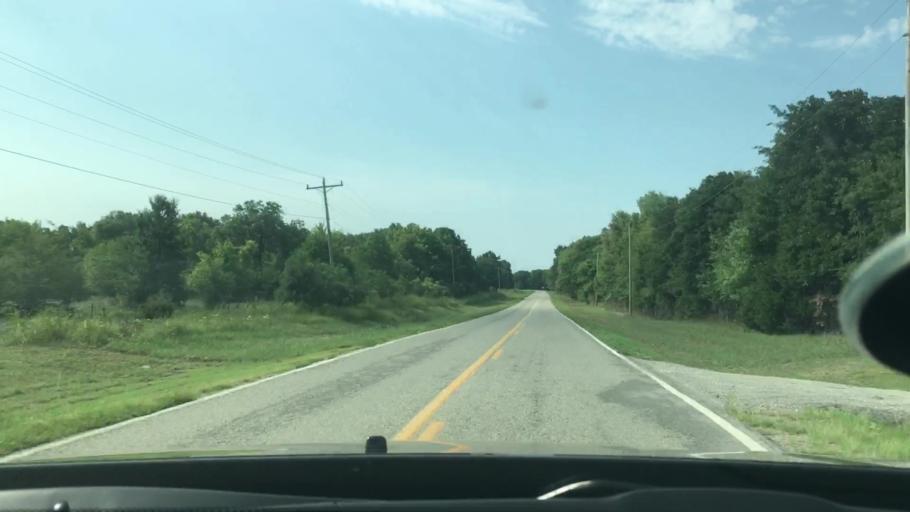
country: US
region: Oklahoma
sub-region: Johnston County
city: Tishomingo
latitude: 34.1743
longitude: -96.5838
